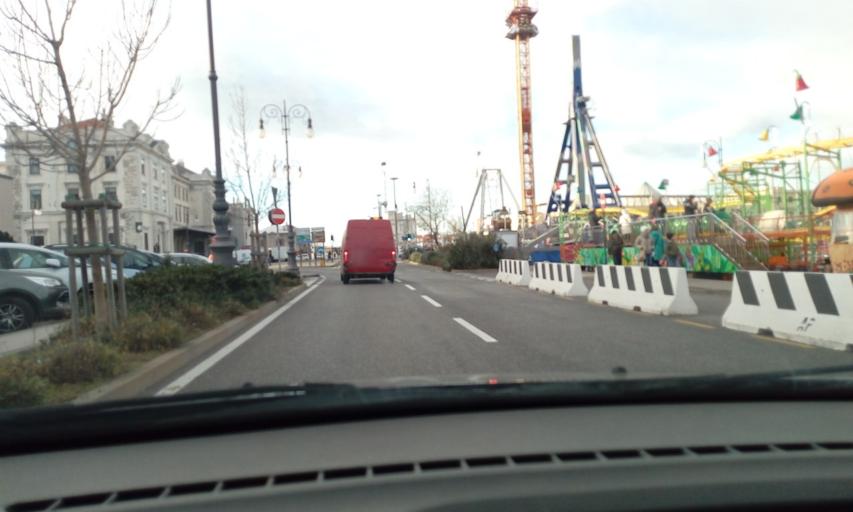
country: IT
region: Friuli Venezia Giulia
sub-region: Provincia di Trieste
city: Trieste
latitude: 45.6461
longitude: 13.7566
